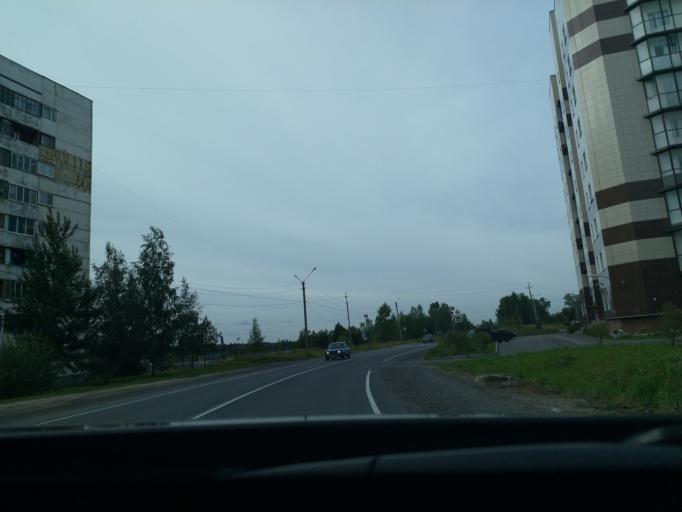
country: RU
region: Leningrad
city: Nikol'skoye
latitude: 59.7101
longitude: 30.7801
